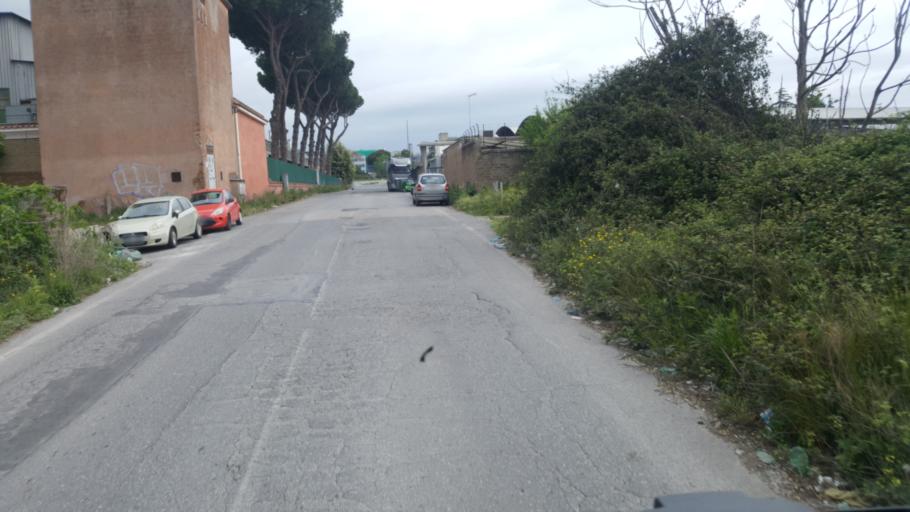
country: IT
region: Latium
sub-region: Citta metropolitana di Roma Capitale
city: Setteville
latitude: 41.9340
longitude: 12.6152
